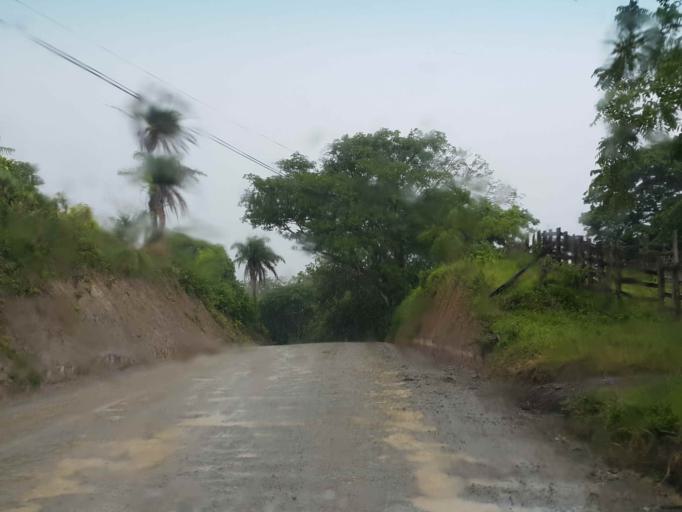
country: CR
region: Guanacaste
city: Juntas
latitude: 10.2333
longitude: -84.8520
